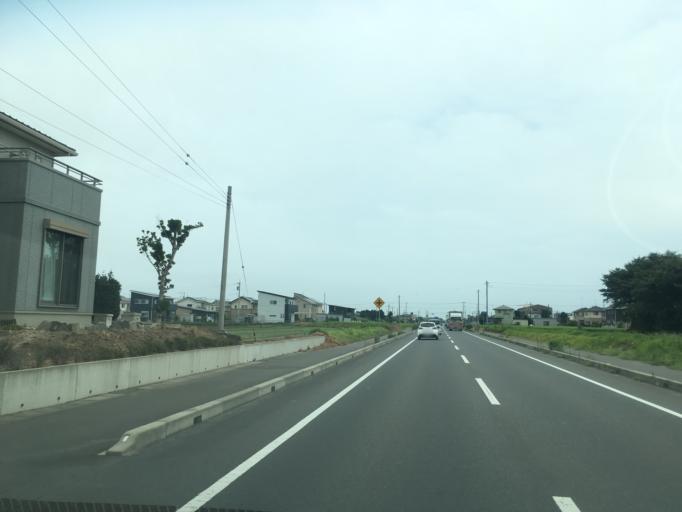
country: JP
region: Ibaraki
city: Hitachi-Naka
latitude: 36.4097
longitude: 140.5757
